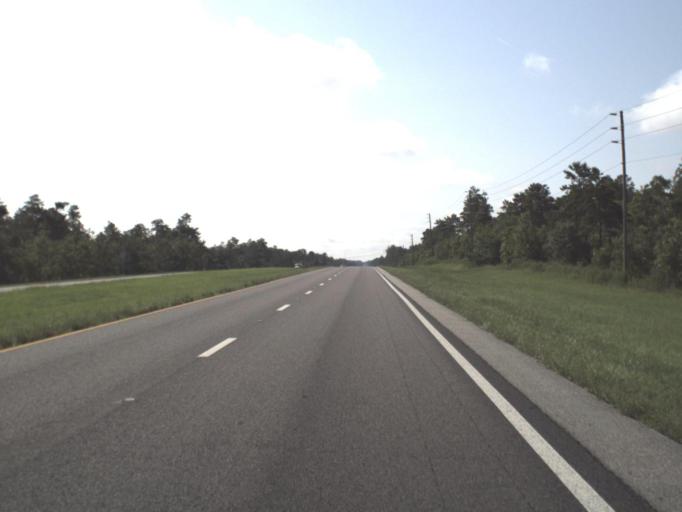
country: US
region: Florida
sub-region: Citrus County
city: Sugarmill Woods
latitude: 28.7014
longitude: -82.5159
